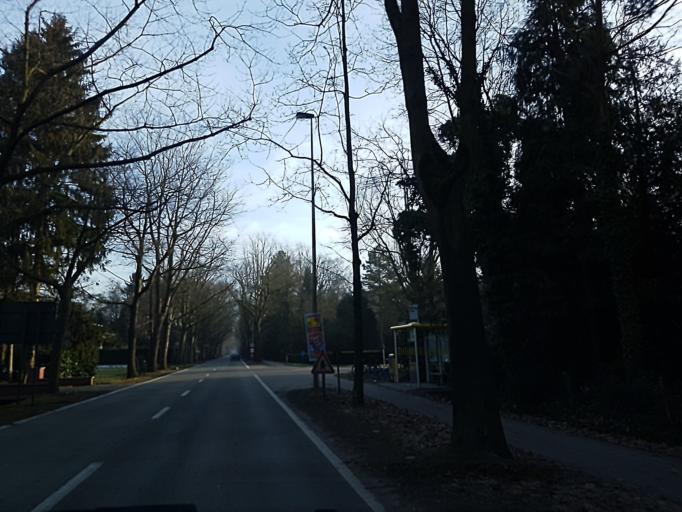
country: BE
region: Flanders
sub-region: Provincie Antwerpen
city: Schilde
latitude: 51.2532
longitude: 4.6172
